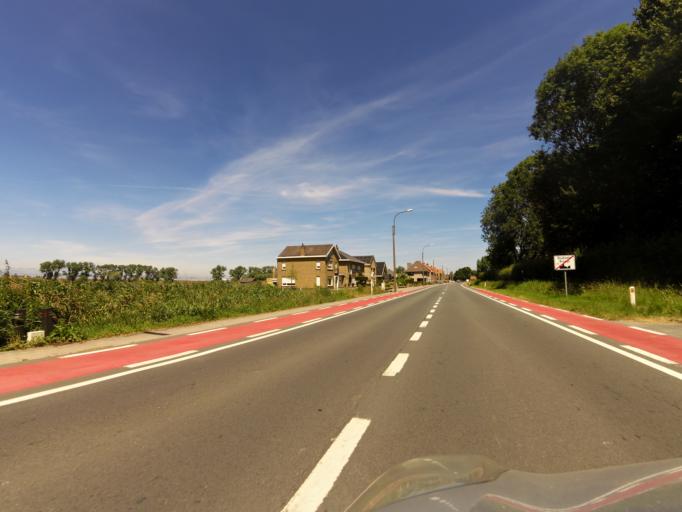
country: BE
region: Flanders
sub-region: Provincie West-Vlaanderen
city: Damme
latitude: 51.2774
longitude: 3.2300
